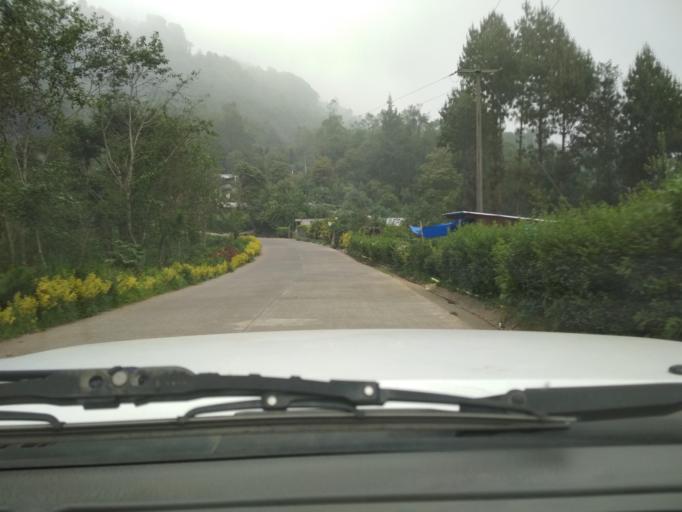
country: MX
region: Veracruz
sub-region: La Perla
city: Chilapa
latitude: 18.9752
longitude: -97.1649
